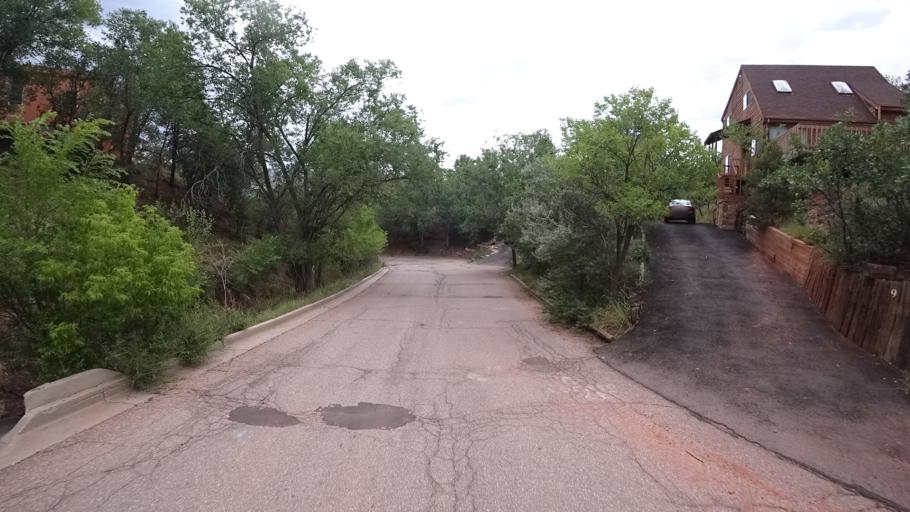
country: US
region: Colorado
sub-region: El Paso County
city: Manitou Springs
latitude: 38.8521
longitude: -104.8938
